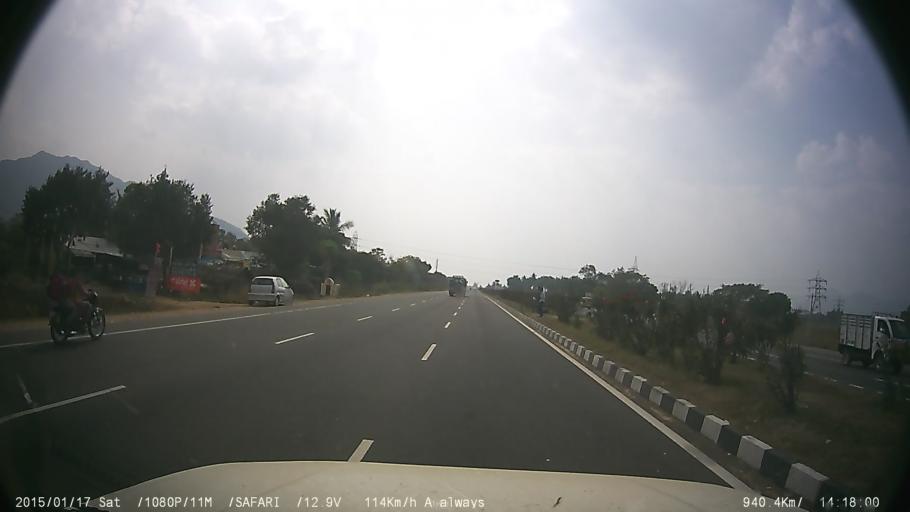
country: IN
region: Tamil Nadu
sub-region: Vellore
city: Ambur
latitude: 12.7348
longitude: 78.6838
